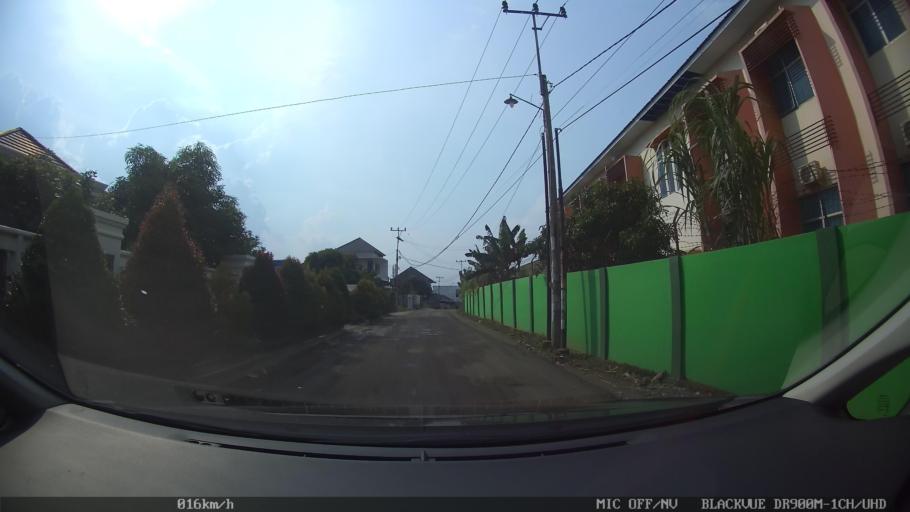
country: ID
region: Lampung
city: Kedaton
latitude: -5.3653
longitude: 105.2185
